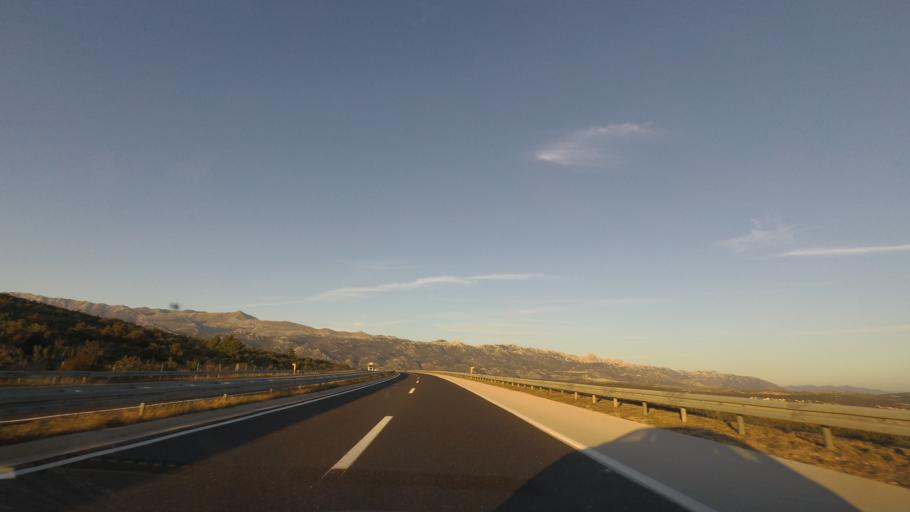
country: HR
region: Zadarska
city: Posedarje
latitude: 44.2225
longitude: 15.5047
